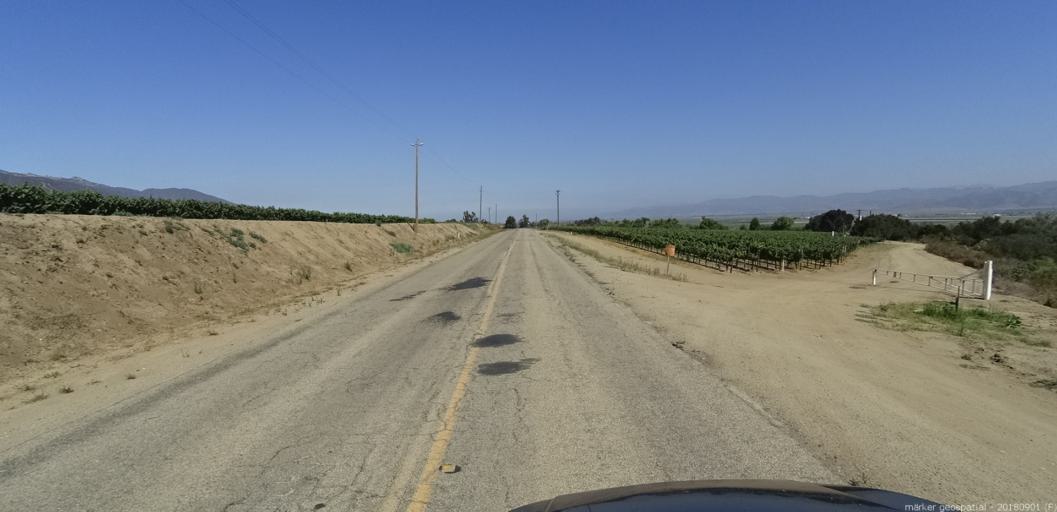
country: US
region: California
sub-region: Monterey County
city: Gonzales
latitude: 36.4861
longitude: -121.4898
